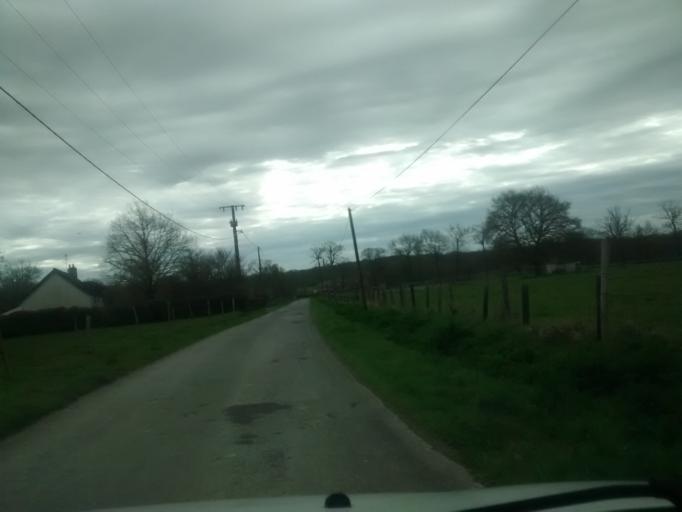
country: FR
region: Brittany
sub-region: Departement d'Ille-et-Vilaine
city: Betton
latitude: 48.1698
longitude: -1.6196
